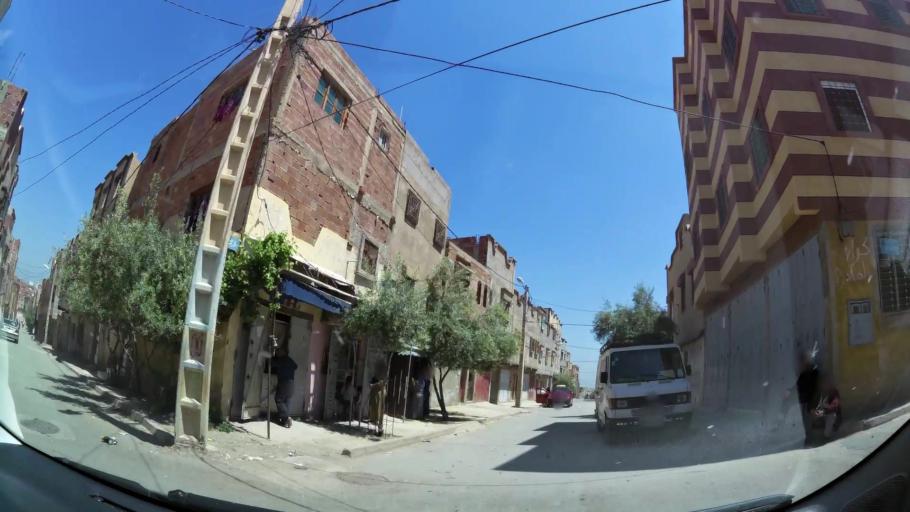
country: MA
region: Oriental
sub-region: Oujda-Angad
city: Oujda
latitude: 34.6788
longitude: -1.9537
